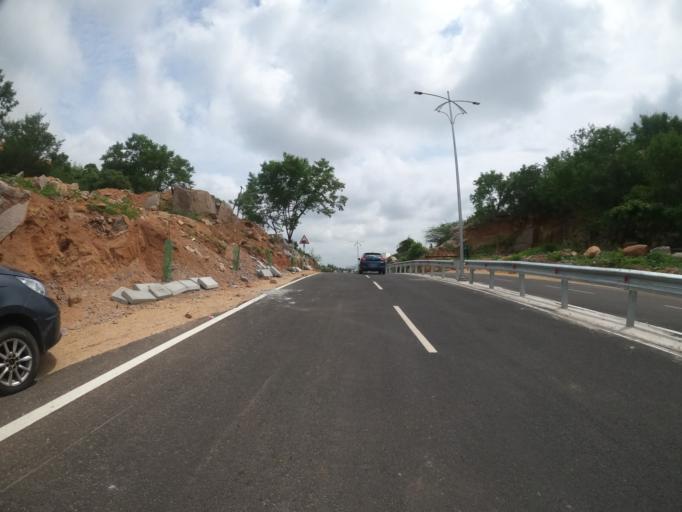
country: IN
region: Telangana
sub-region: Rangareddi
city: Kukatpalli
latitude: 17.4198
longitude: 78.3982
